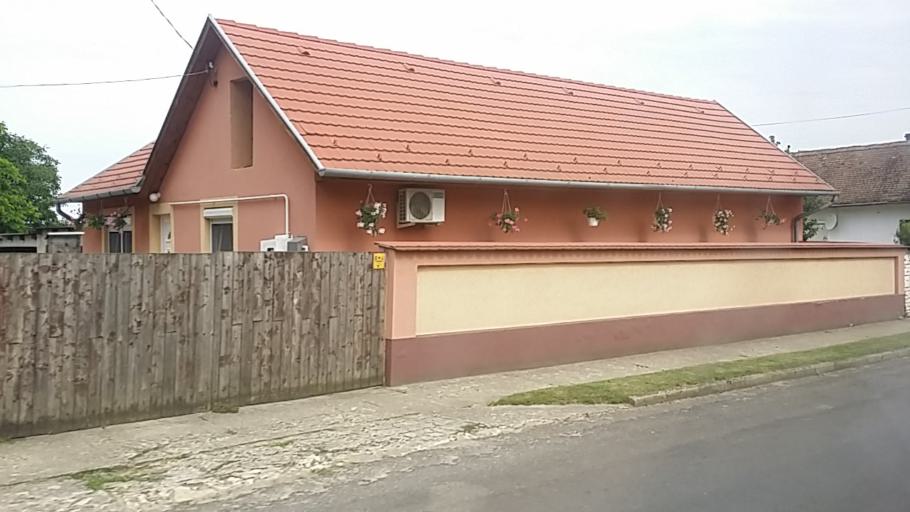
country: HU
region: Baranya
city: Villany
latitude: 45.9080
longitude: 18.4706
